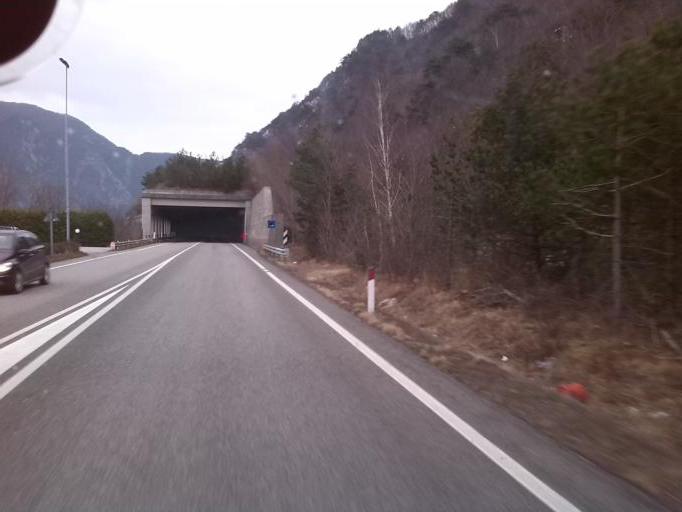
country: IT
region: Friuli Venezia Giulia
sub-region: Provincia di Udine
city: Venzone
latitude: 46.3675
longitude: 13.1350
